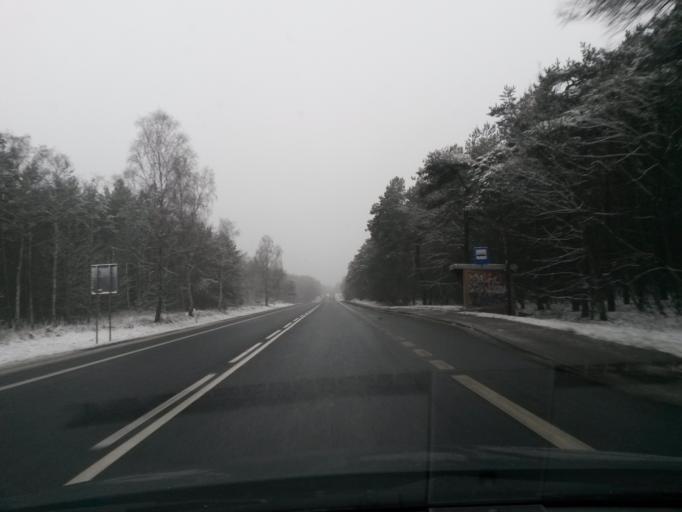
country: PL
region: Kujawsko-Pomorskie
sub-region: Powiat bydgoski
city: Biale Blota
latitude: 53.1572
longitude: 17.8834
